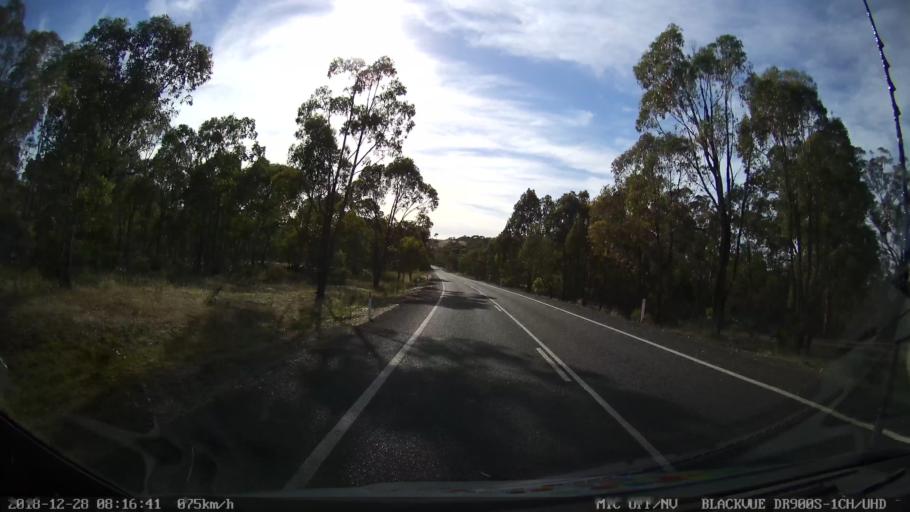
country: AU
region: New South Wales
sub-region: Blayney
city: Blayney
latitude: -33.8357
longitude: 149.3313
